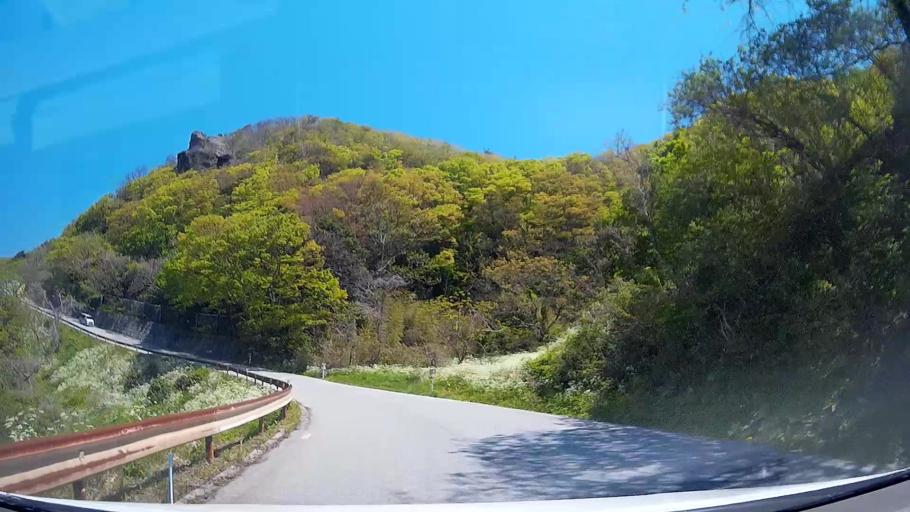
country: JP
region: Ishikawa
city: Nanao
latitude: 37.5239
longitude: 137.2566
